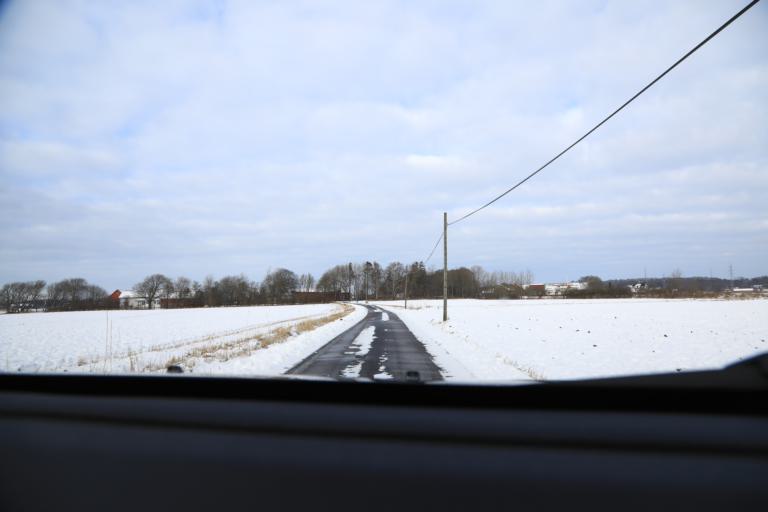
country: SE
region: Halland
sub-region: Kungsbacka Kommun
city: Frillesas
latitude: 57.2285
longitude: 12.1894
